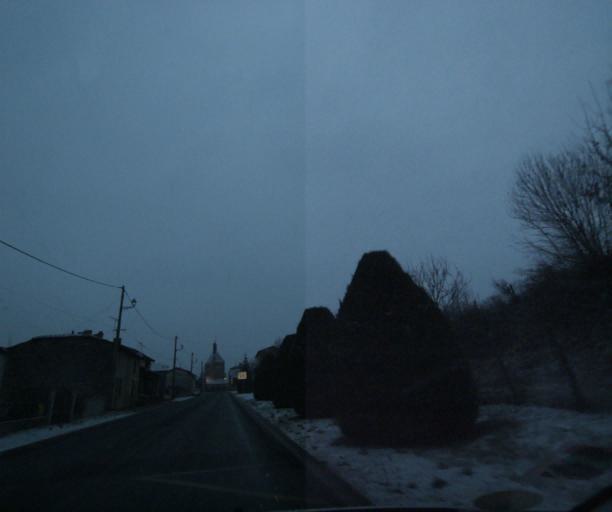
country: FR
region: Champagne-Ardenne
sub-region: Departement de la Haute-Marne
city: Wassy
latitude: 48.4259
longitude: 4.9610
